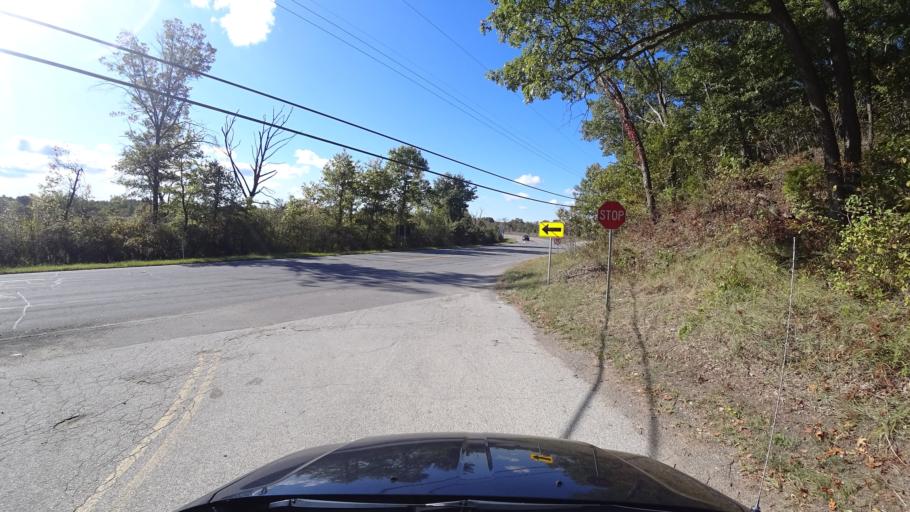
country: US
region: Indiana
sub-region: LaPorte County
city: Michigan City
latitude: 41.7057
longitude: -86.9310
